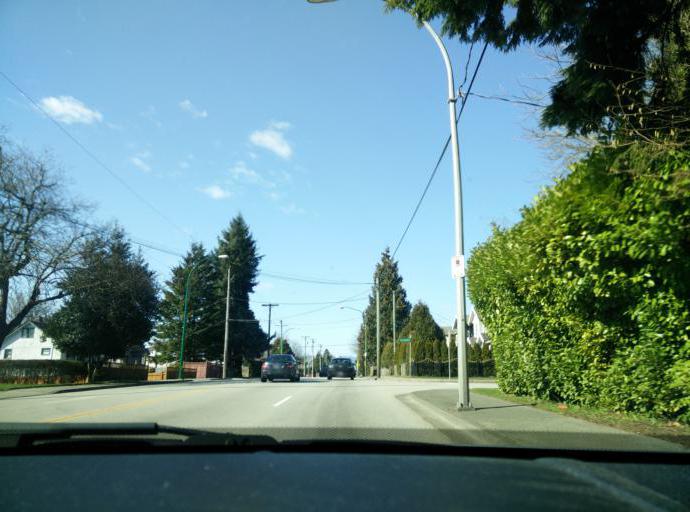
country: CA
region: British Columbia
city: New Westminster
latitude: 49.2209
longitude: -122.9367
